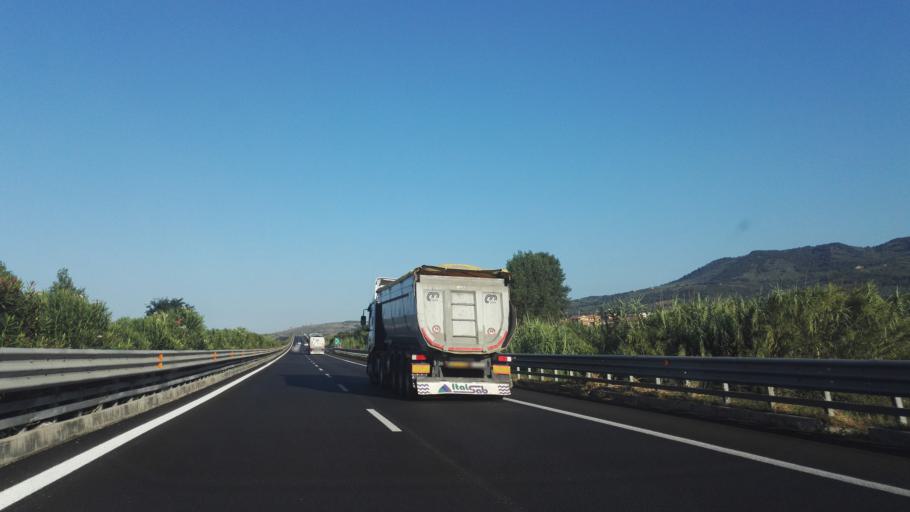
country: IT
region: Calabria
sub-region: Provincia di Catanzaro
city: Santa Eufemia Lamezia
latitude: 38.9359
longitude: 16.2152
